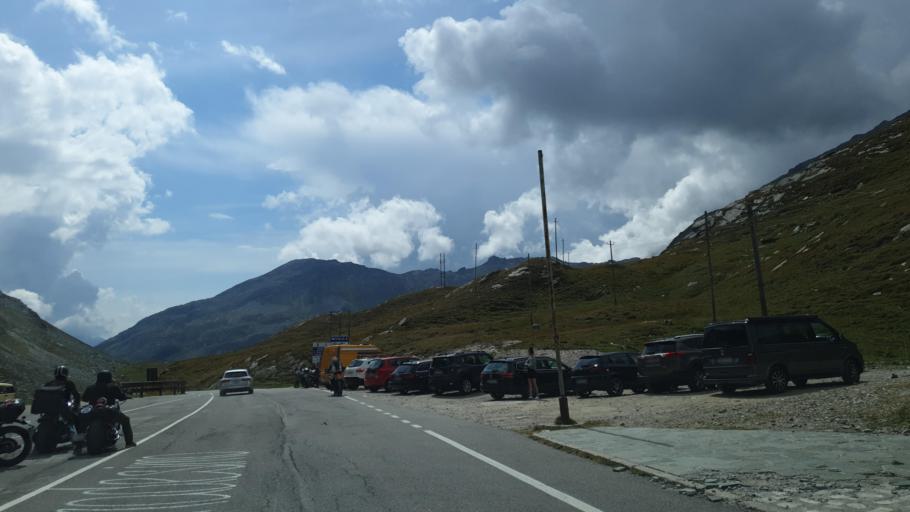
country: IT
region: Lombardy
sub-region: Provincia di Sondrio
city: Campodolcino
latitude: 46.5052
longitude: 9.3303
